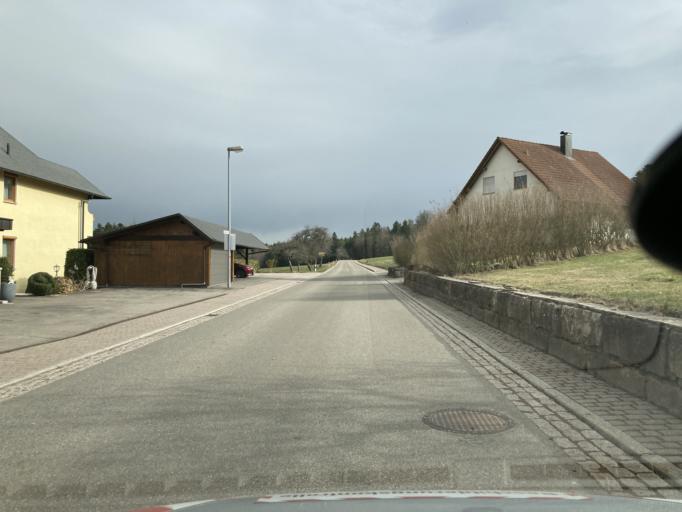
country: DE
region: Baden-Wuerttemberg
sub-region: Karlsruhe Region
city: Neuweiler
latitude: 48.6759
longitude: 8.6210
